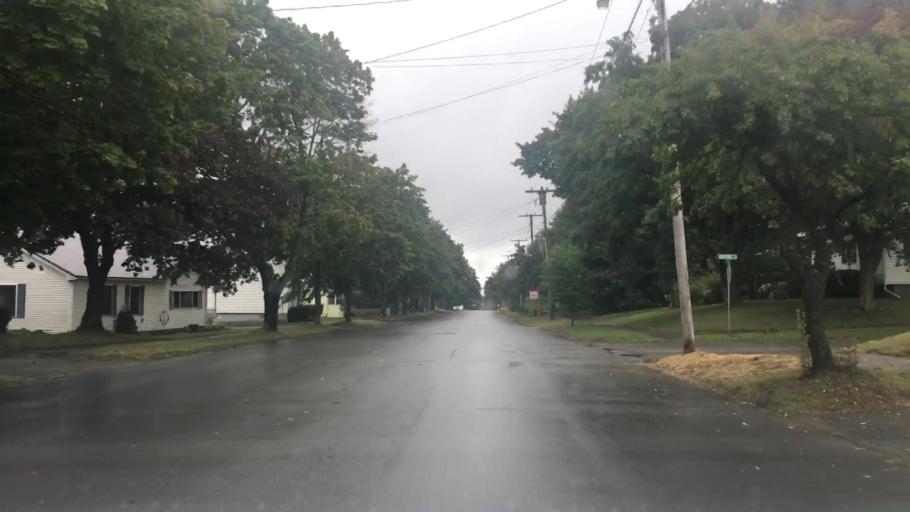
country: US
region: Maine
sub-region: Penobscot County
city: Brewer
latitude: 44.8171
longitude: -68.7604
